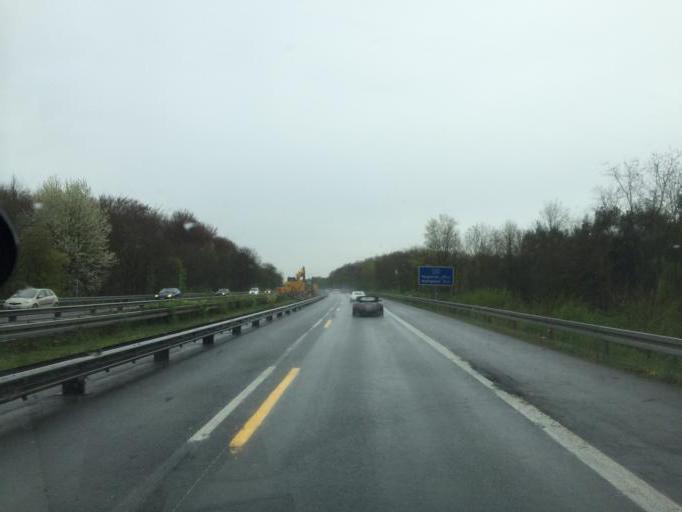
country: DE
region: North Rhine-Westphalia
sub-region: Regierungsbezirk Munster
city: Haltern
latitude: 51.6958
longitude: 7.1476
